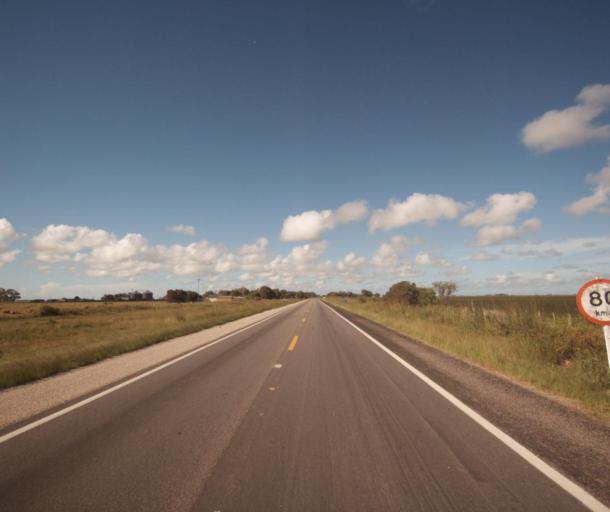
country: UY
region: Cerro Largo
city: Rio Branco
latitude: -33.0391
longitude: -52.8609
